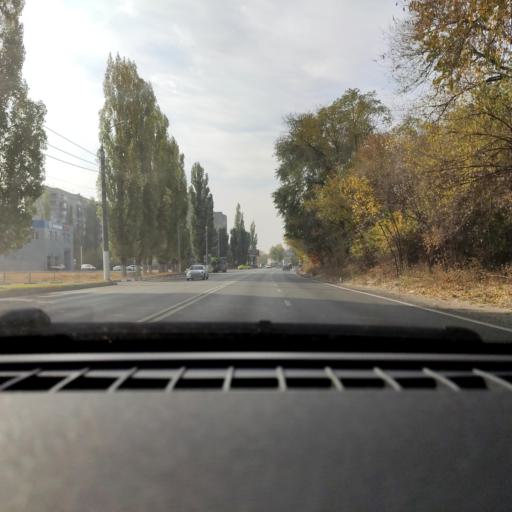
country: RU
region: Voronezj
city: Maslovka
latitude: 51.6024
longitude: 39.2536
